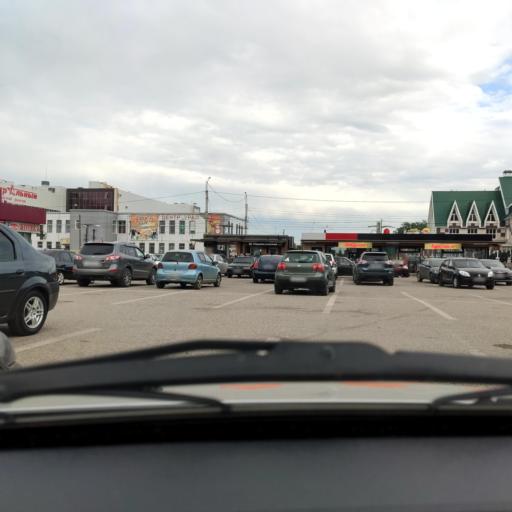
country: RU
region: Bashkortostan
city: Sterlitamak
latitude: 53.6127
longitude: 55.9532
